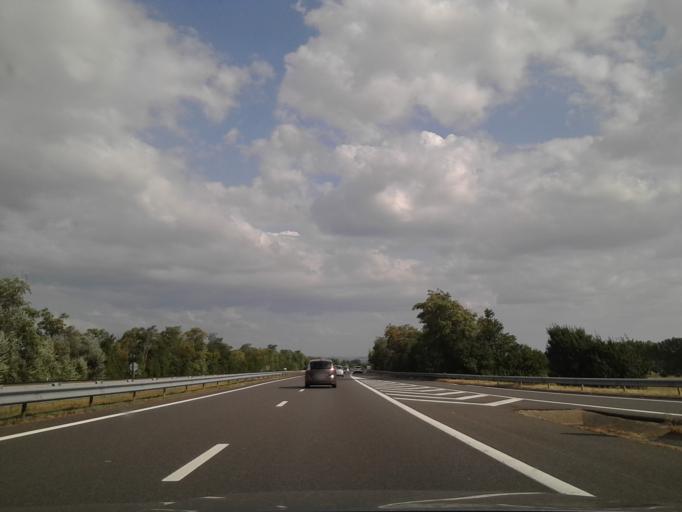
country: FR
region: Auvergne
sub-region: Departement du Puy-de-Dome
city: Saint-Bonnet-pres-Riom
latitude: 45.9204
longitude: 3.1471
